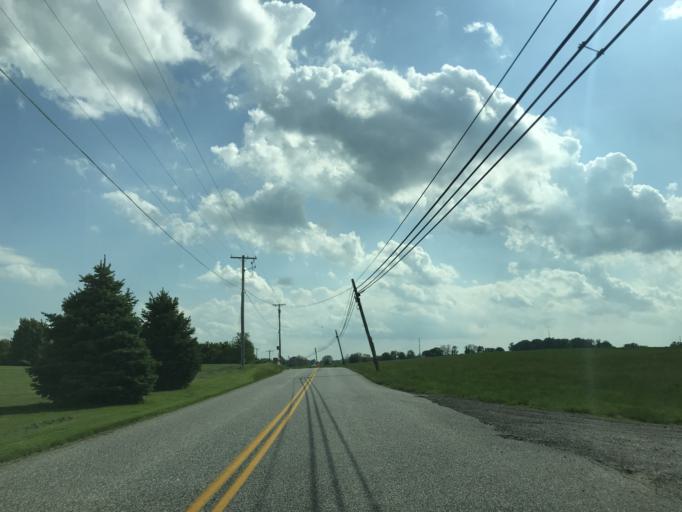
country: US
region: Maryland
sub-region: Harford County
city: Bel Air North
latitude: 39.6031
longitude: -76.3734
